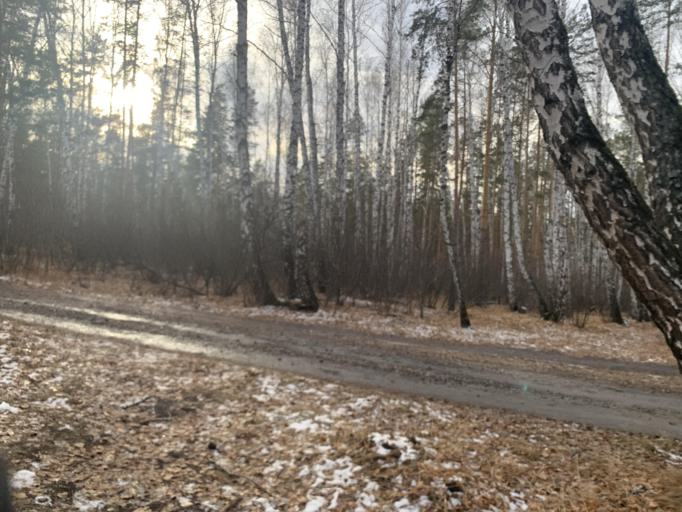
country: RU
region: Chelyabinsk
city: Roshchino
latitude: 55.2001
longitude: 61.3007
